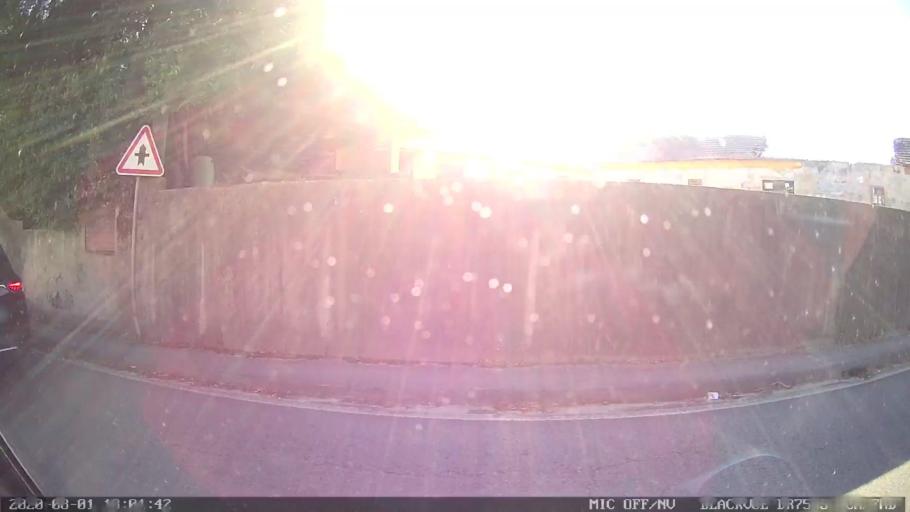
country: PT
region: Porto
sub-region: Santo Tirso
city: Santo Tirso
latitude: 41.3485
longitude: -8.4665
